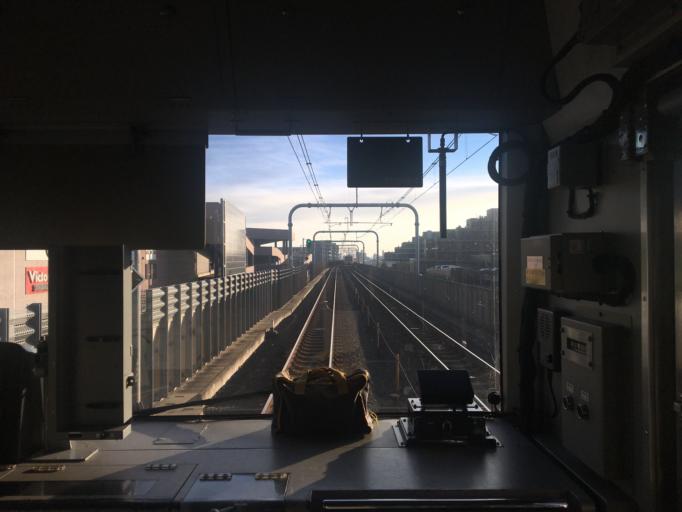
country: JP
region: Saitama
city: Yoshikawa
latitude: 35.8763
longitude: 139.8231
